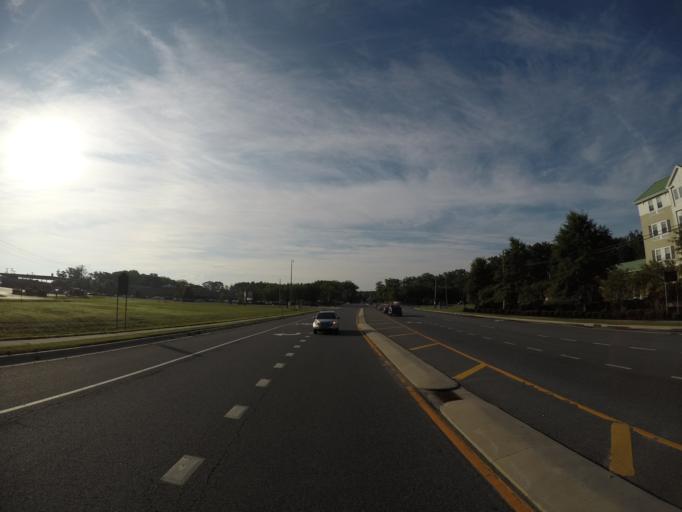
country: US
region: Delaware
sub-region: Sussex County
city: Ocean View
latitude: 38.4708
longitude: -75.1168
